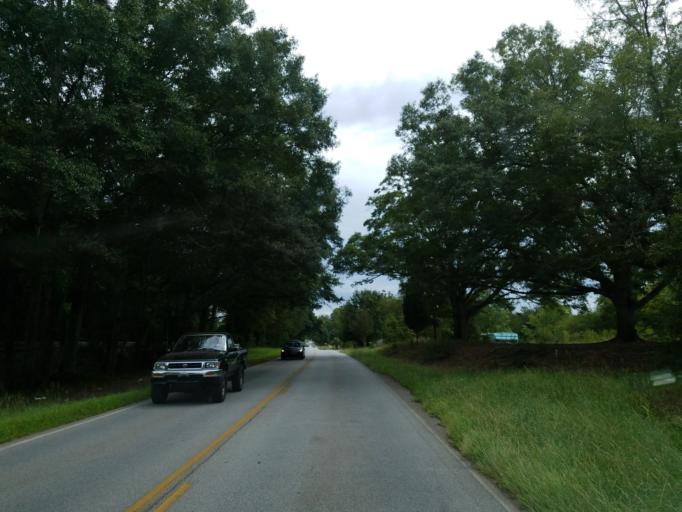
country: US
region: Georgia
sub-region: Spalding County
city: Experiment
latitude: 33.2895
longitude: -84.2855
